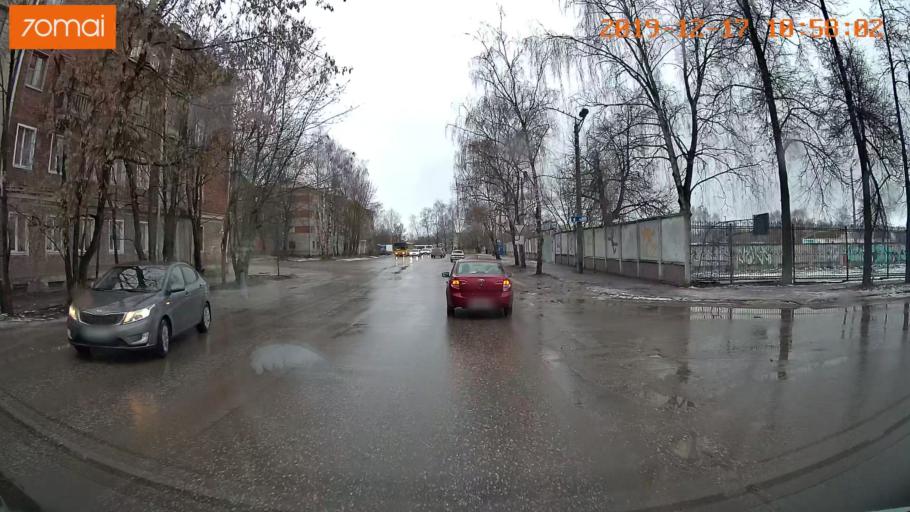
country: RU
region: Vladimir
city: Gus'-Khrustal'nyy
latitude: 55.6222
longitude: 40.6548
